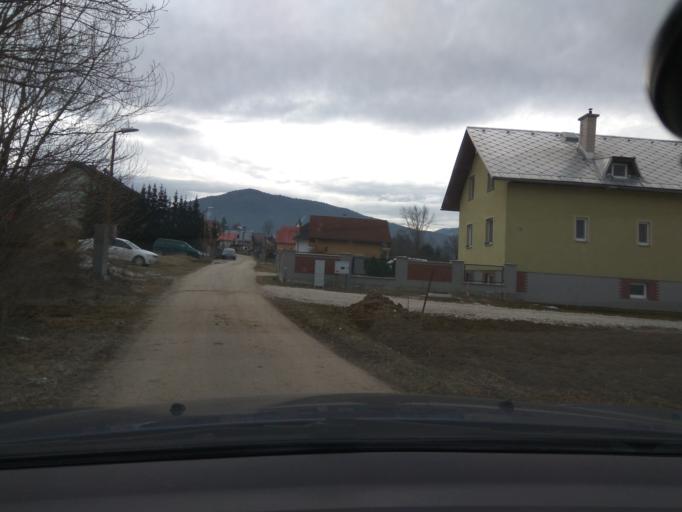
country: SK
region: Zilinsky
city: Rajec
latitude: 49.1018
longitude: 18.6878
